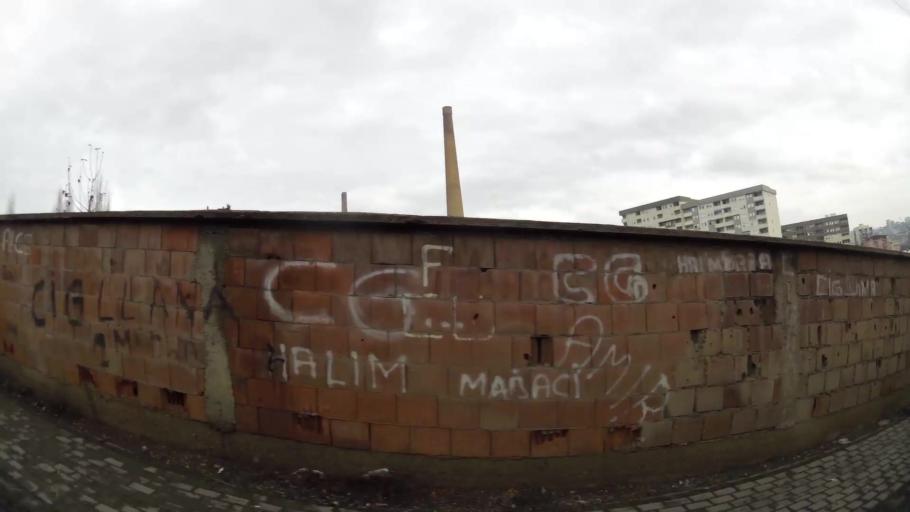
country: XK
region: Pristina
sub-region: Komuna e Prishtines
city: Pristina
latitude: 42.6699
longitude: 21.1575
